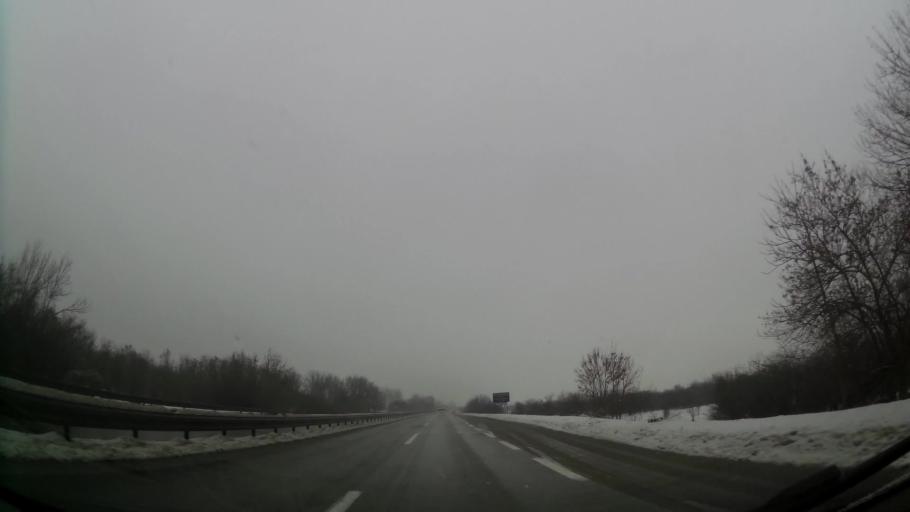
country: RS
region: Central Serbia
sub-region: Belgrade
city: Cukarica
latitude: 44.7600
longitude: 20.3867
